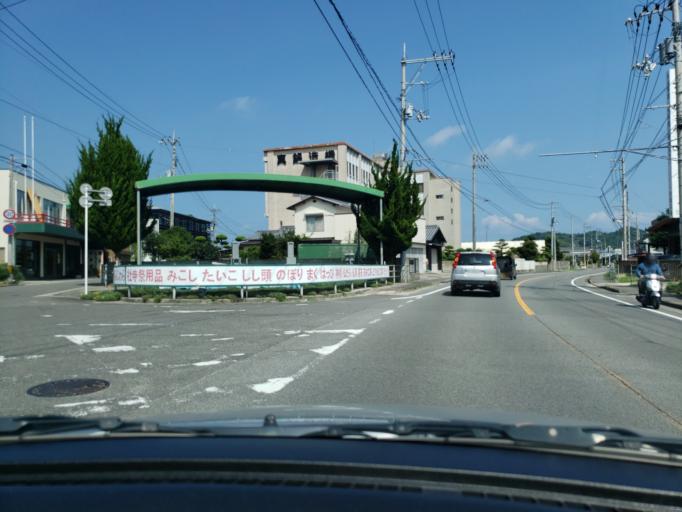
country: JP
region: Ehime
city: Hojo
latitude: 34.0959
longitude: 132.9736
